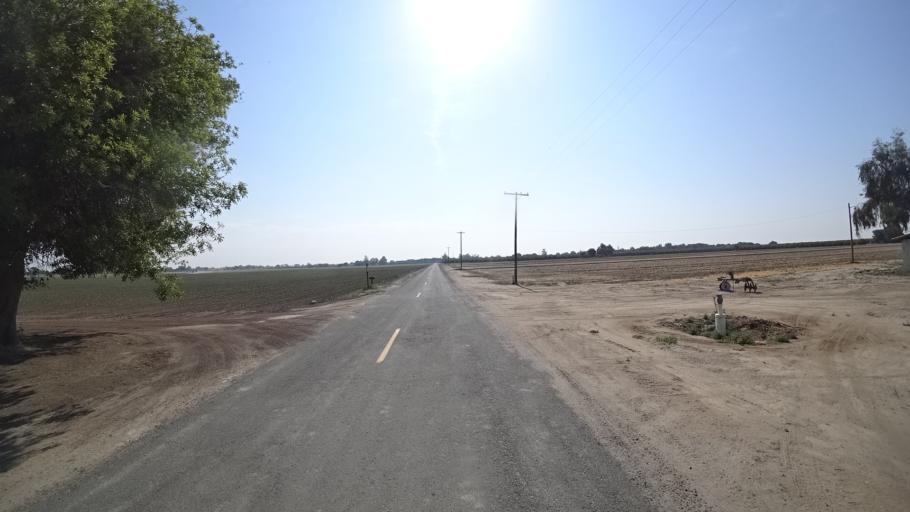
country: US
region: California
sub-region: Kings County
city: Lemoore Station
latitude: 36.3367
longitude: -119.8648
